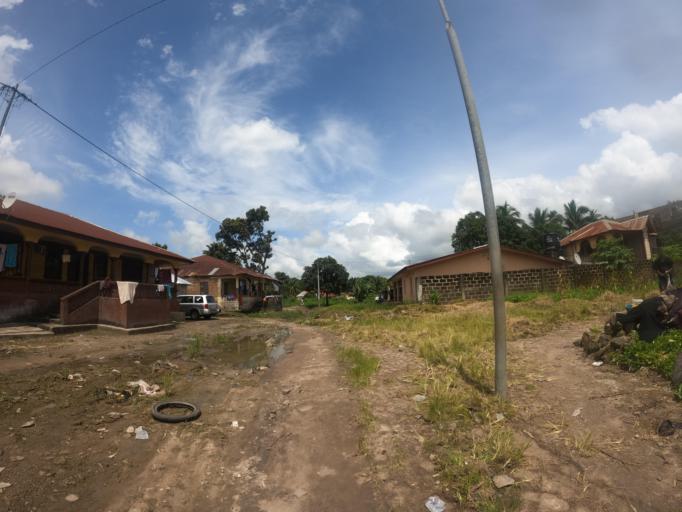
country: SL
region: Northern Province
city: Makeni
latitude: 8.8897
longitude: -12.0522
